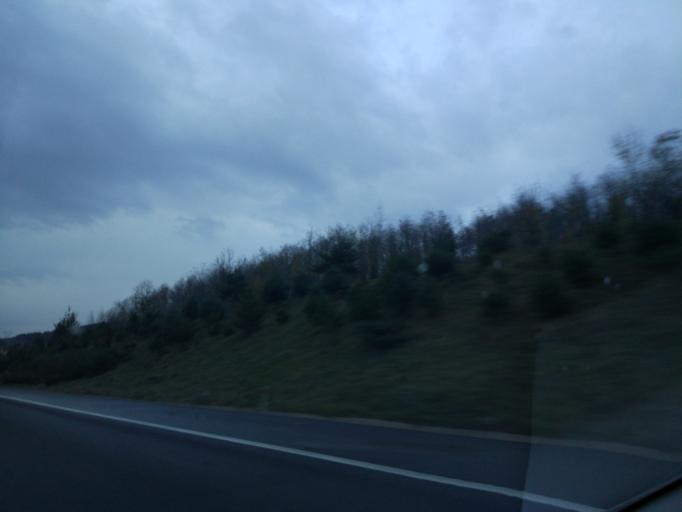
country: TR
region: Duzce
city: Kaynasli
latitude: 40.7789
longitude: 31.3495
